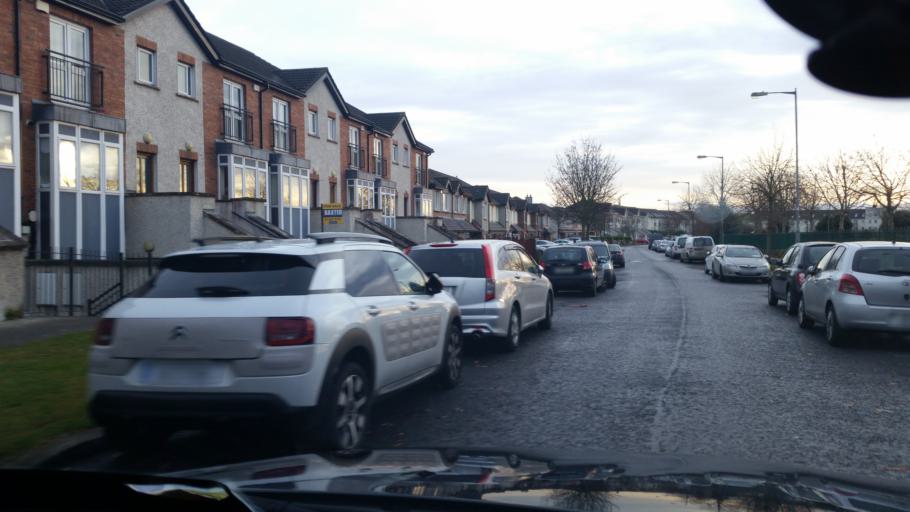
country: IE
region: Leinster
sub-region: Dublin City
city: Finglas
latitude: 53.4046
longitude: -6.2950
